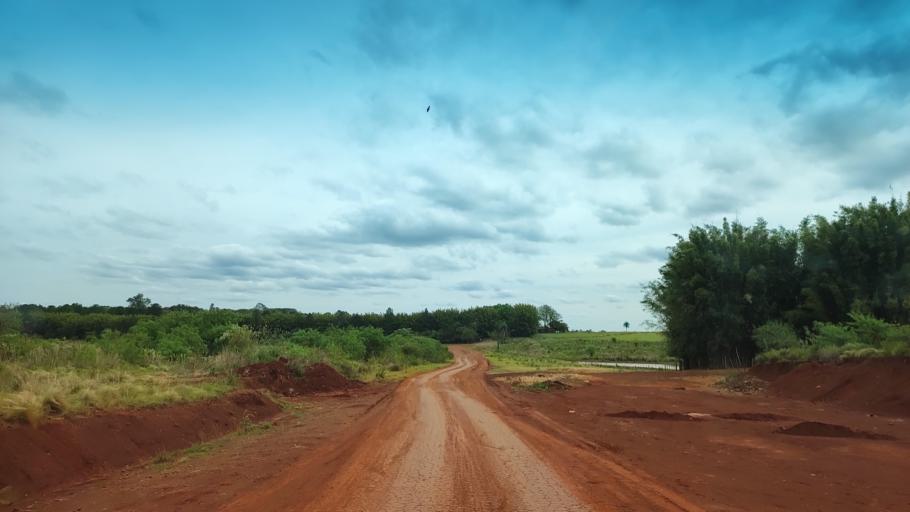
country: AR
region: Misiones
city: Garupa
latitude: -27.5158
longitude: -55.9723
